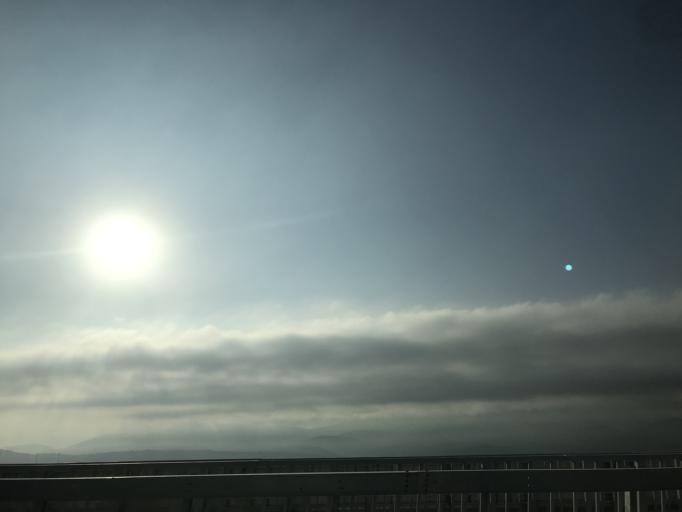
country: TR
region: Balikesir
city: Susurluk
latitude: 39.9598
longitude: 28.1534
